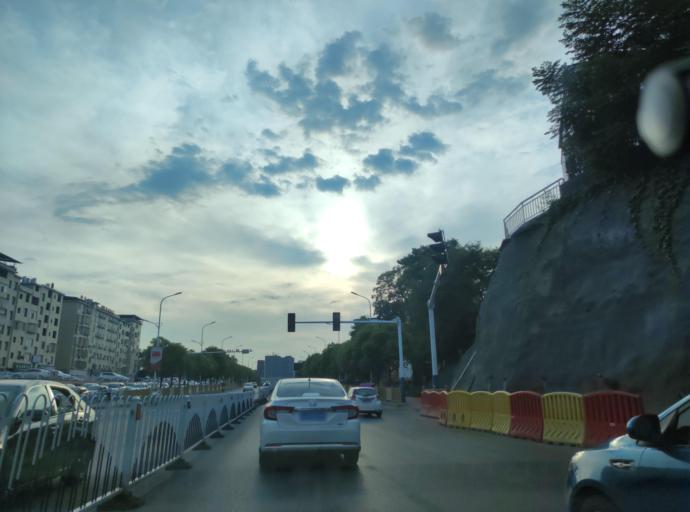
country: CN
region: Jiangxi Sheng
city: Pingxiang
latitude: 27.6338
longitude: 113.8636
